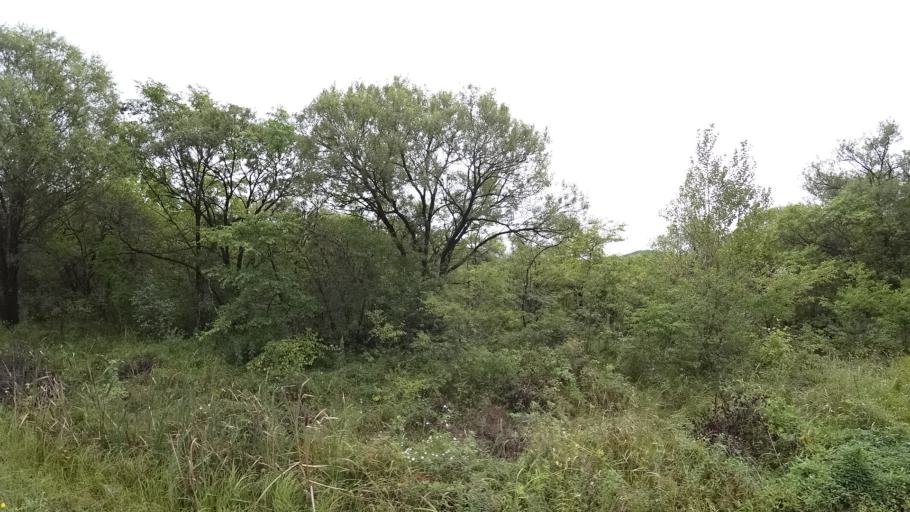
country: RU
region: Primorskiy
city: Lyalichi
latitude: 44.0760
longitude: 132.4596
